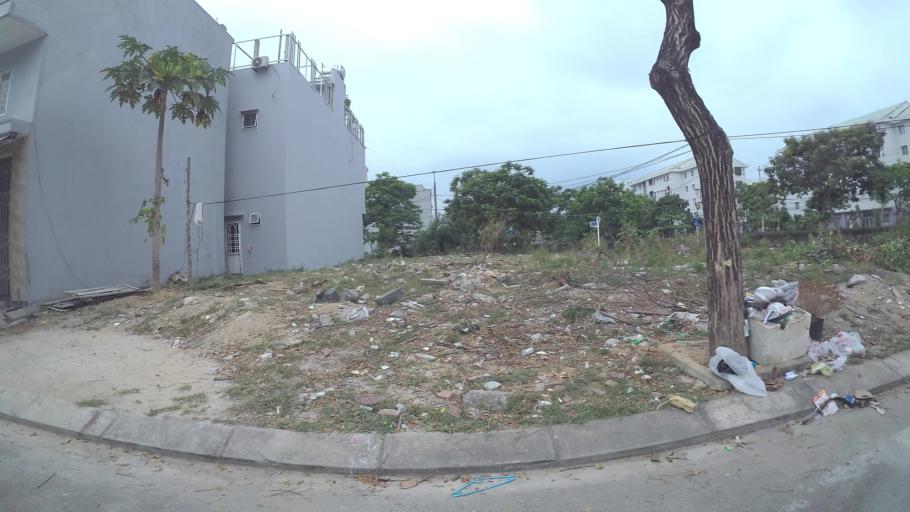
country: VN
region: Da Nang
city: Lien Chieu
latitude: 16.0734
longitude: 108.1687
